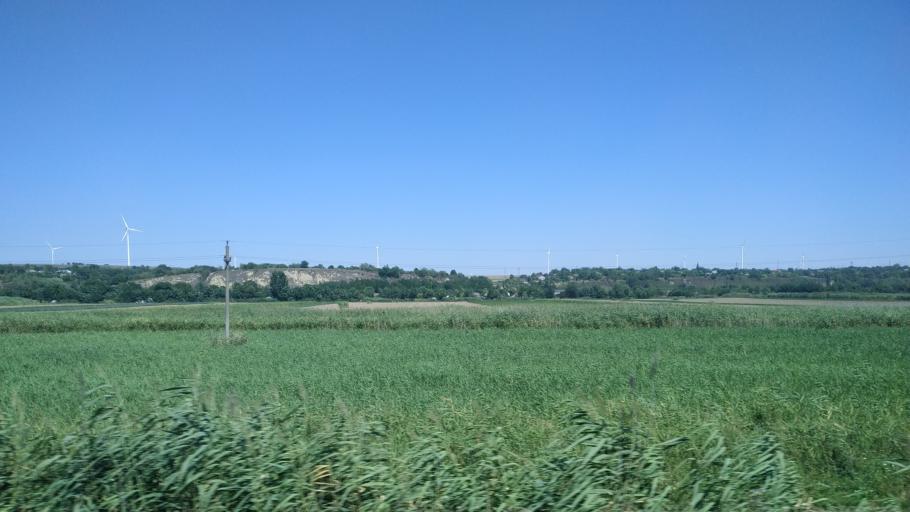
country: RO
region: Constanta
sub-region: Comuna Saligny
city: Faclia
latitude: 44.2734
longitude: 28.0989
